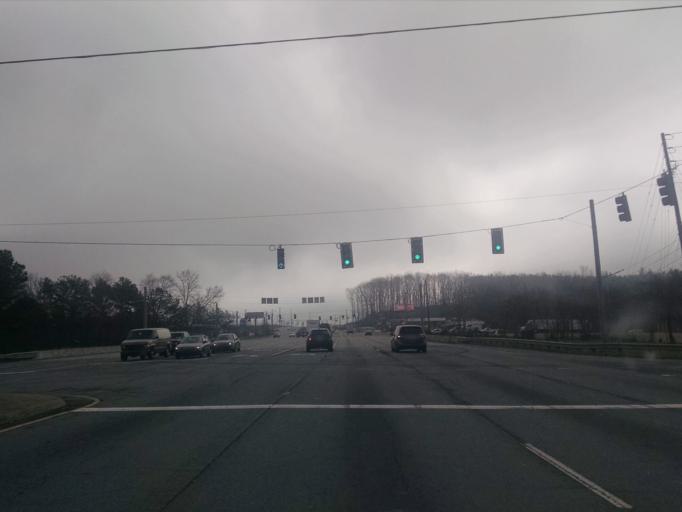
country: US
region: Georgia
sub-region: Gwinnett County
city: Buford
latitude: 34.0877
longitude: -83.9945
